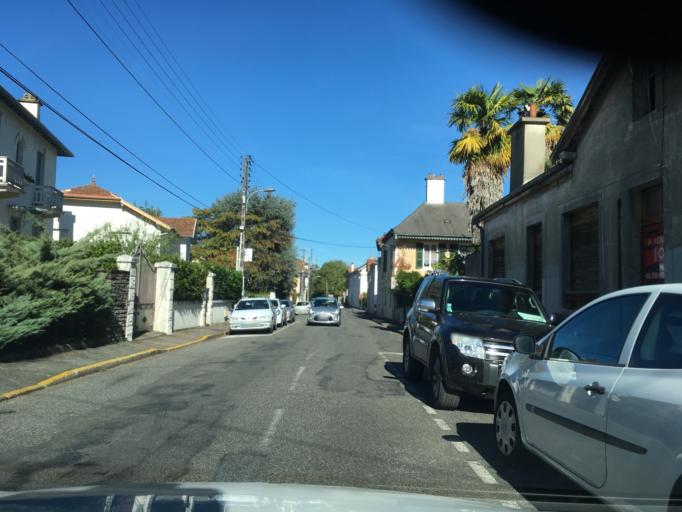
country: FR
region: Aquitaine
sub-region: Departement des Pyrenees-Atlantiques
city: Pau
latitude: 43.3100
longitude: -0.3760
